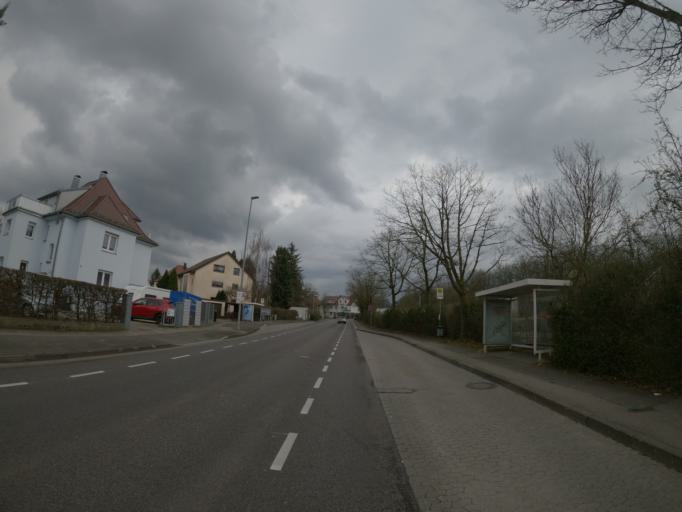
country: DE
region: Baden-Wuerttemberg
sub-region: Regierungsbezirk Stuttgart
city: Eislingen
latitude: 48.6890
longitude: 9.6833
